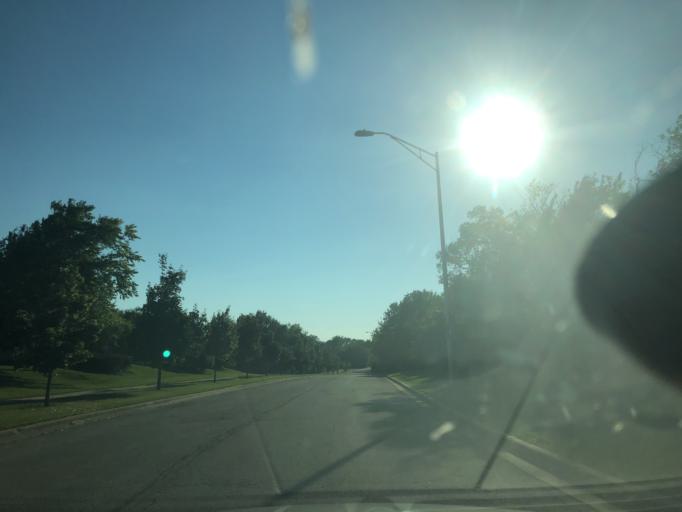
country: US
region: Illinois
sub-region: Will County
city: Mokena
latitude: 41.5569
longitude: -87.8982
